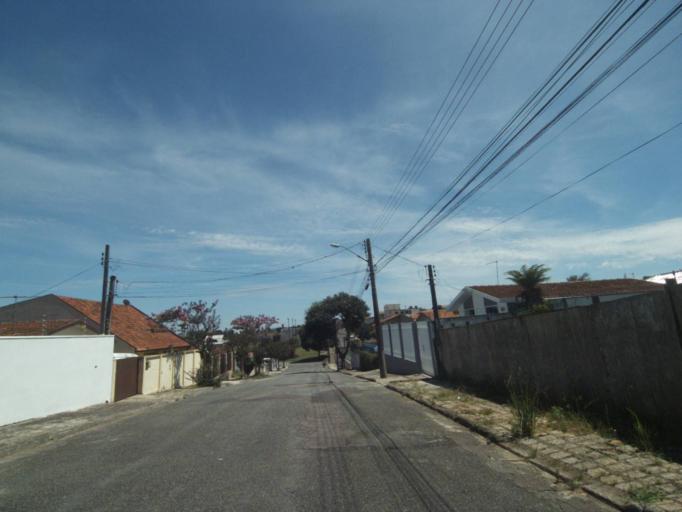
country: BR
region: Parana
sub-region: Curitiba
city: Curitiba
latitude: -25.4667
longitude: -49.2393
